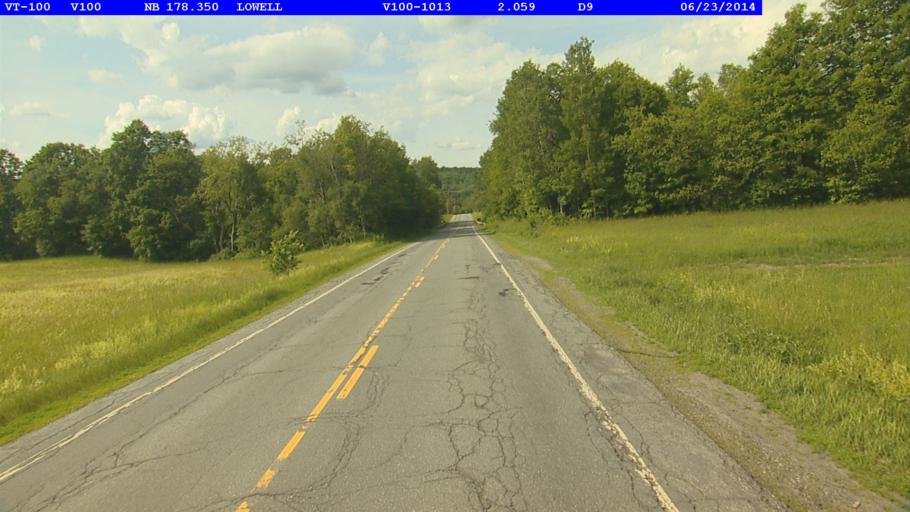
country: US
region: Vermont
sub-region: Lamoille County
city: Hyde Park
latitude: 44.7678
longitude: -72.4571
